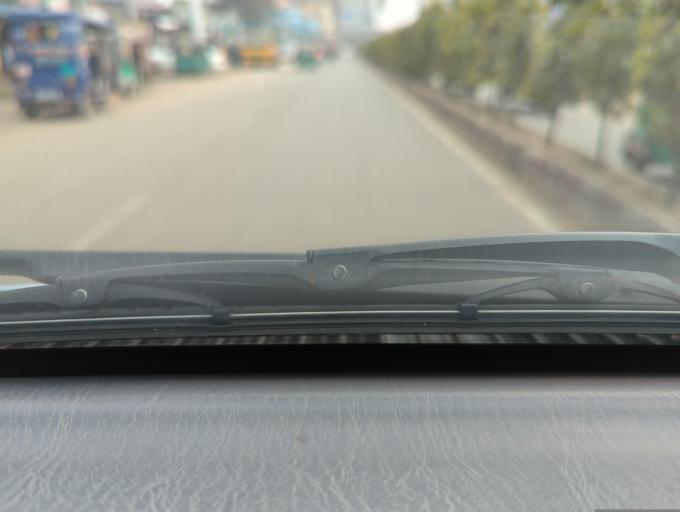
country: BD
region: Sylhet
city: Maulavi Bazar
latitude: 24.4893
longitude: 91.7622
